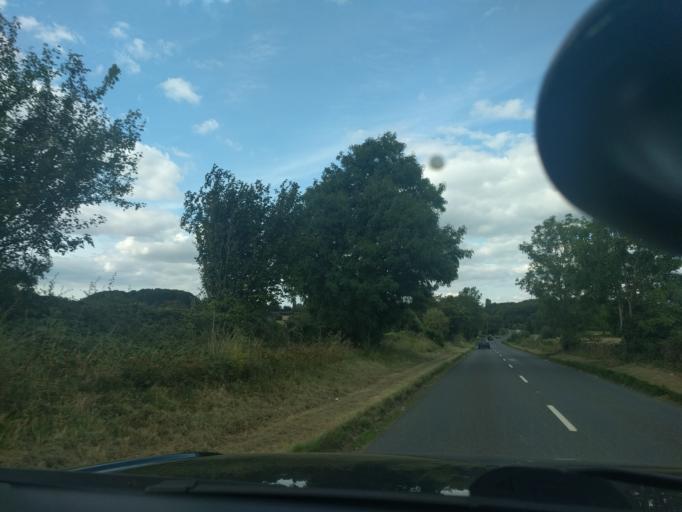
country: GB
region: England
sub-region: Wiltshire
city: Box
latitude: 51.4127
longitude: -2.2302
